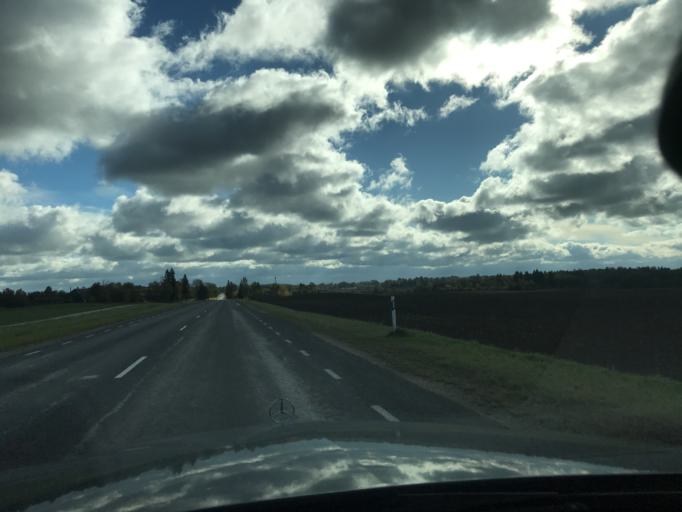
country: EE
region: Vorumaa
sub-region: Antsla vald
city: Vana-Antsla
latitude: 57.9516
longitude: 26.2850
